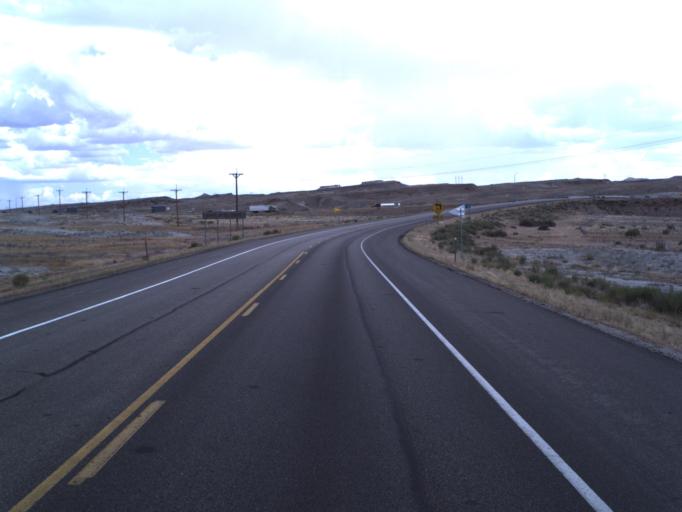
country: US
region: Utah
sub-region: Carbon County
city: East Carbon City
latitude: 38.9806
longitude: -110.1224
